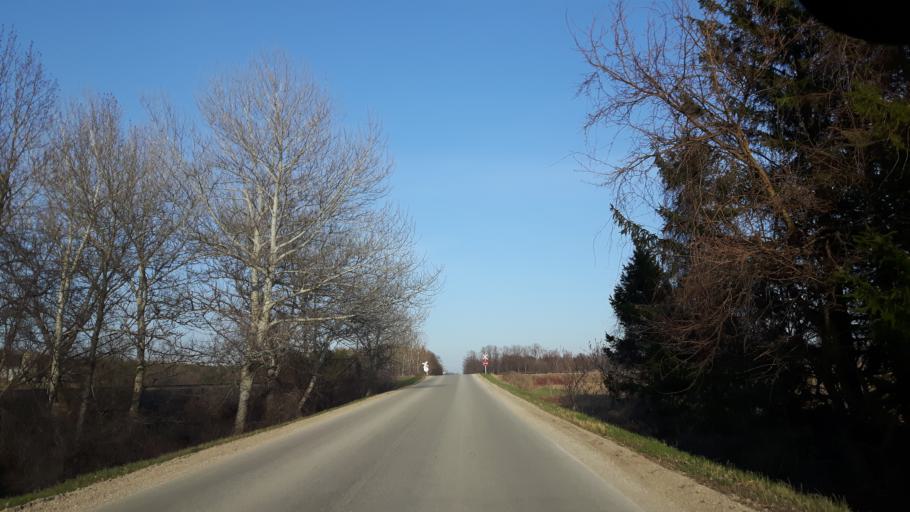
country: CA
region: Ontario
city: Goderich
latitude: 43.6985
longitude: -81.6844
